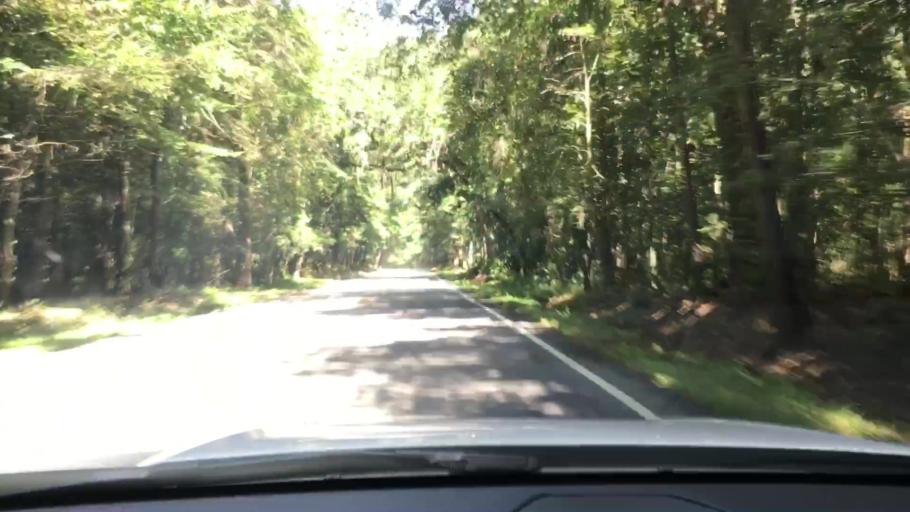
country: US
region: South Carolina
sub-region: Berkeley County
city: Hanahan
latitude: 32.8863
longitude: -80.1137
